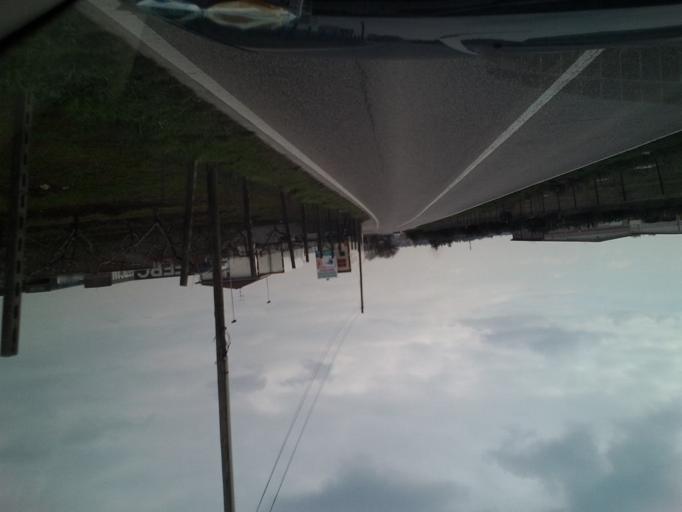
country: IT
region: Veneto
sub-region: Provincia di Verona
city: Caselle
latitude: 45.4089
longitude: 10.8730
